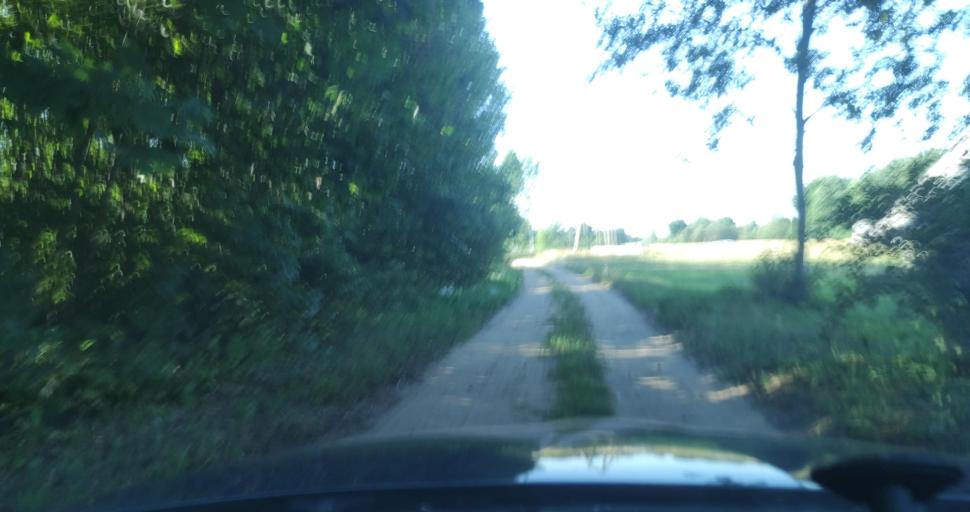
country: LV
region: Skrunda
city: Skrunda
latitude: 56.6650
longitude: 22.0269
